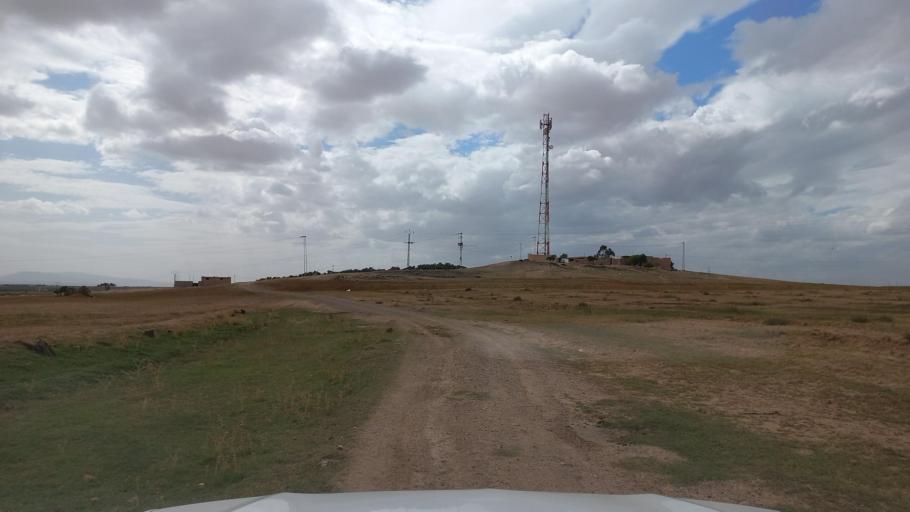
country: TN
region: Al Qasrayn
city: Sbiba
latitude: 35.3793
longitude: 9.0981
